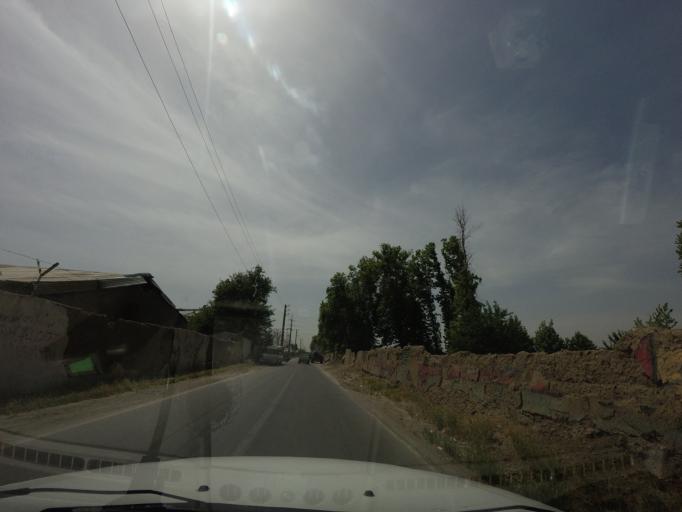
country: IR
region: Tehran
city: Eslamshahr
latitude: 35.6564
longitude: 51.2538
